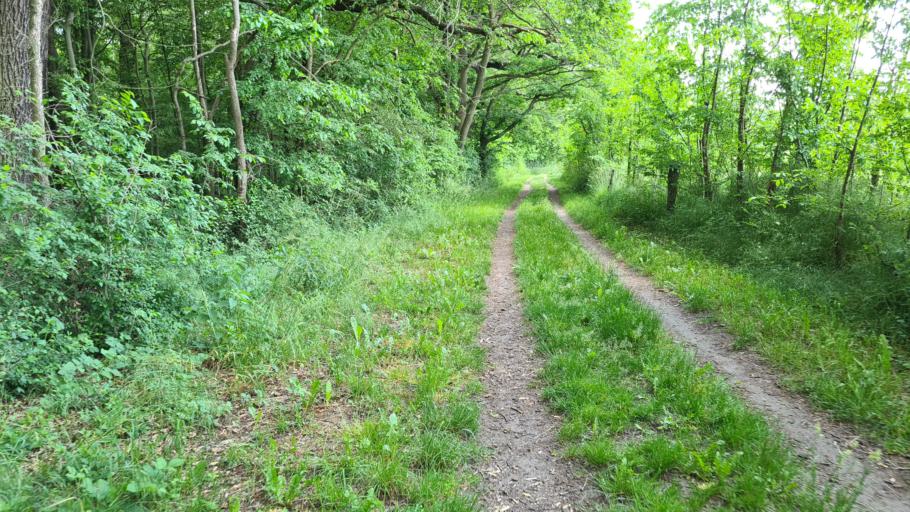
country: DE
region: Brandenburg
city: Sonnewalde
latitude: 51.7007
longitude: 13.6364
